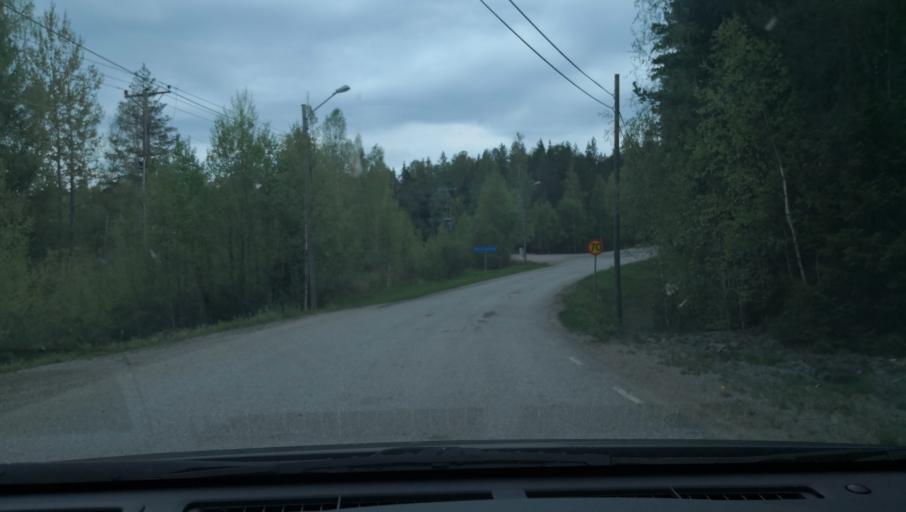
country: SE
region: Vaestmanland
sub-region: Skinnskattebergs Kommun
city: Skinnskatteberg
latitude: 59.8301
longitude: 15.5595
